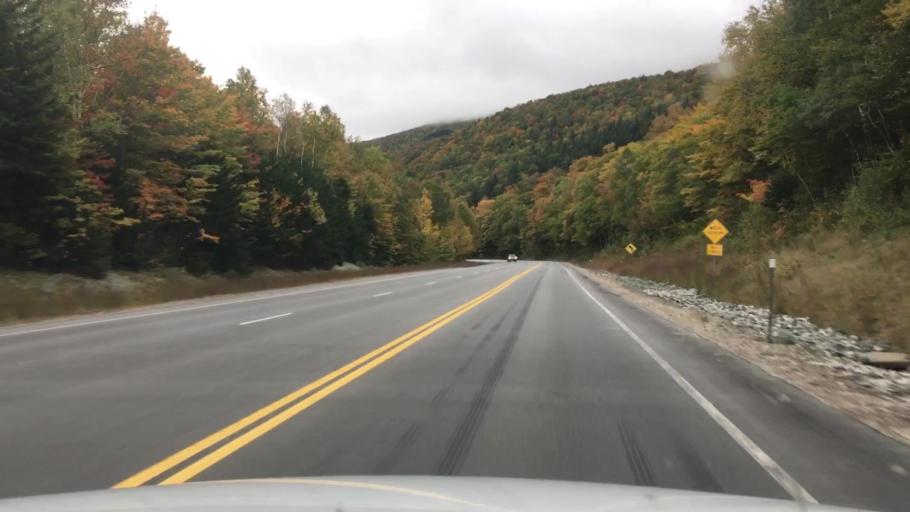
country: US
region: New Hampshire
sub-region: Coos County
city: Gorham
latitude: 44.2368
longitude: -71.2570
